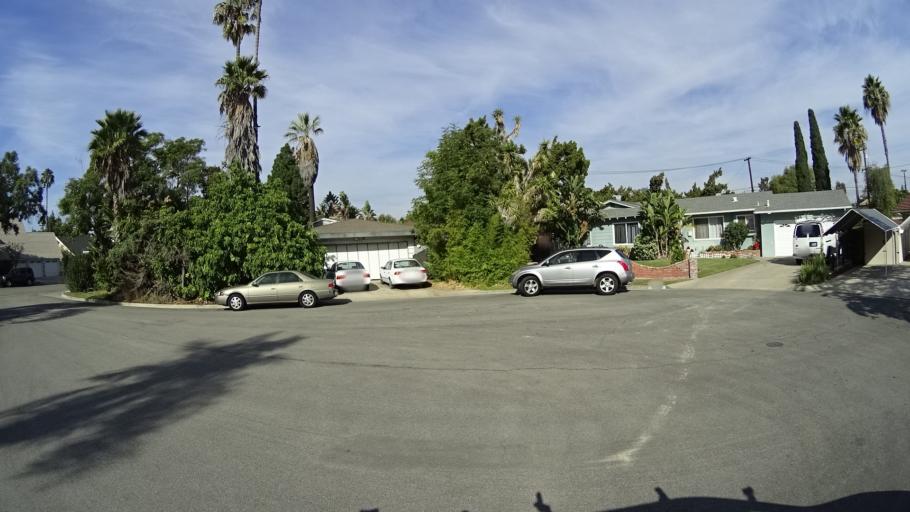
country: US
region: California
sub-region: Orange County
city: Garden Grove
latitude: 33.7919
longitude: -117.9382
